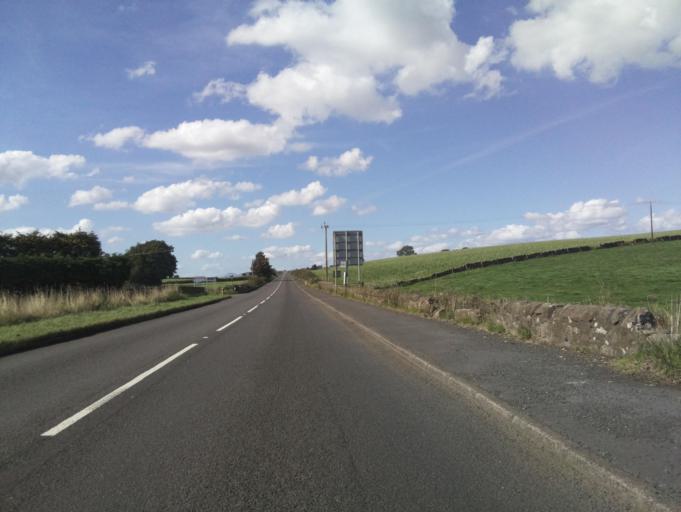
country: GB
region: Scotland
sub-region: Stirling
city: Plean
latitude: 56.0735
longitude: -3.8857
